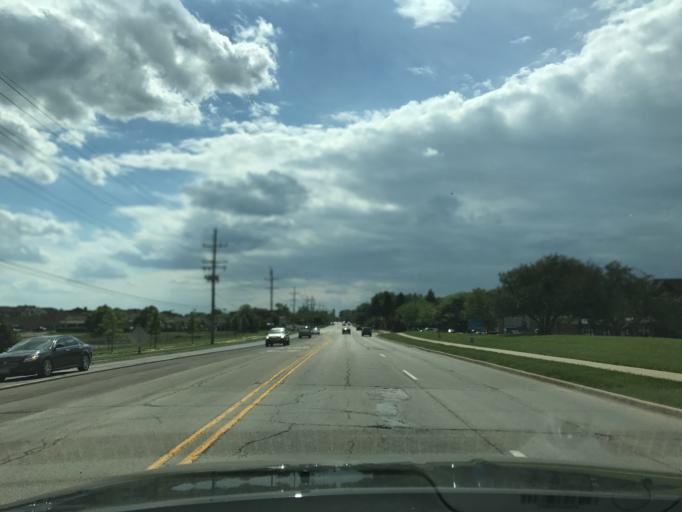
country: US
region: Illinois
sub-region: DuPage County
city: Lisle
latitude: 41.7810
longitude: -88.1019
